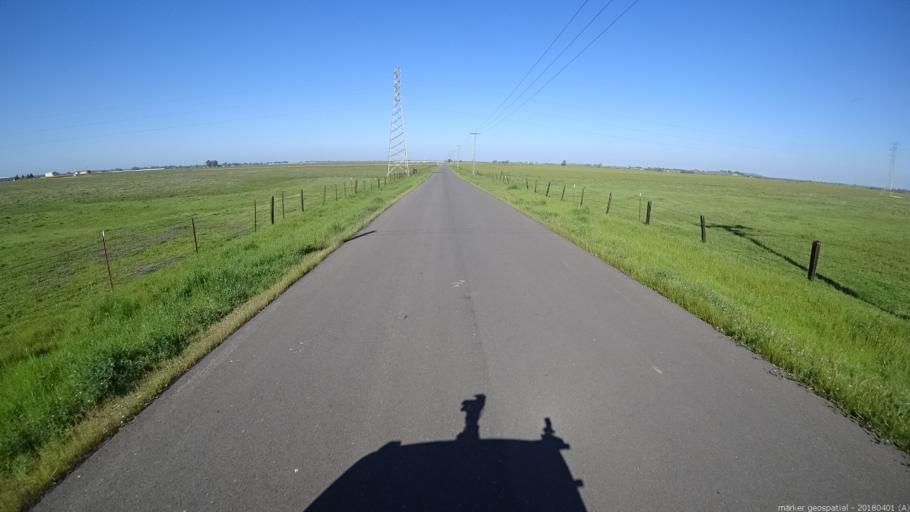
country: US
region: California
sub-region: Sacramento County
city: Rancho Murieta
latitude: 38.4651
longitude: -121.1405
